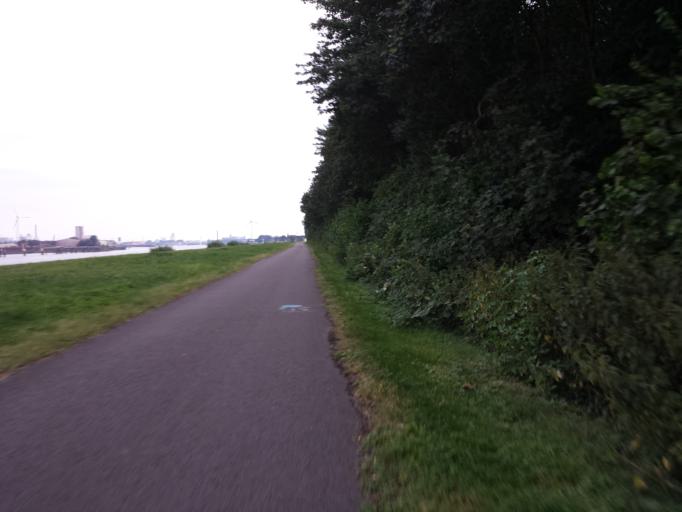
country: DE
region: Lower Saxony
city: Lemwerder
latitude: 53.1224
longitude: 8.6736
